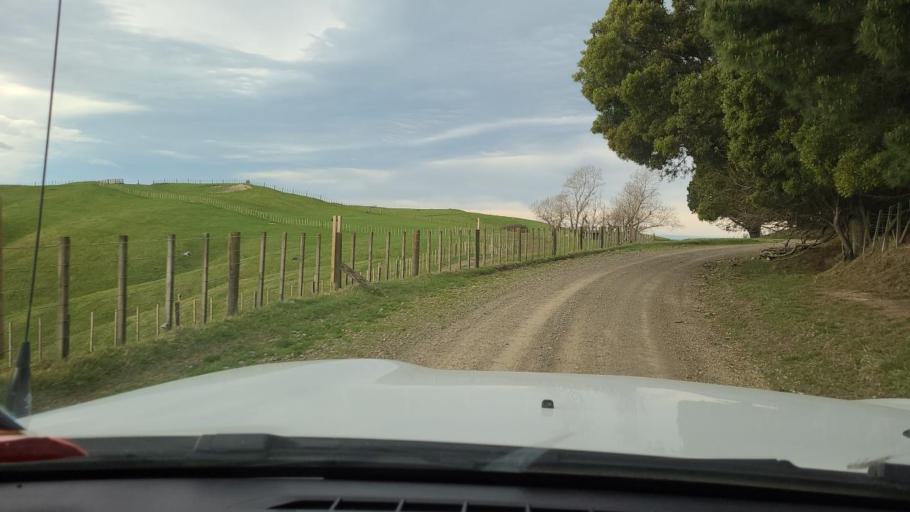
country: NZ
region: Hawke's Bay
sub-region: Napier City
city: Napier
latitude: -39.2254
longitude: 177.0076
